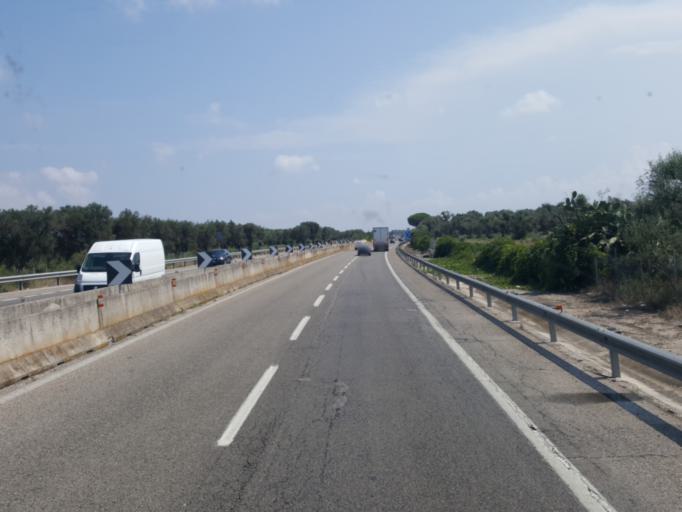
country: IT
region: Apulia
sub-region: Provincia di Brindisi
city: Torchiarolo
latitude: 40.4970
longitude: 18.0345
